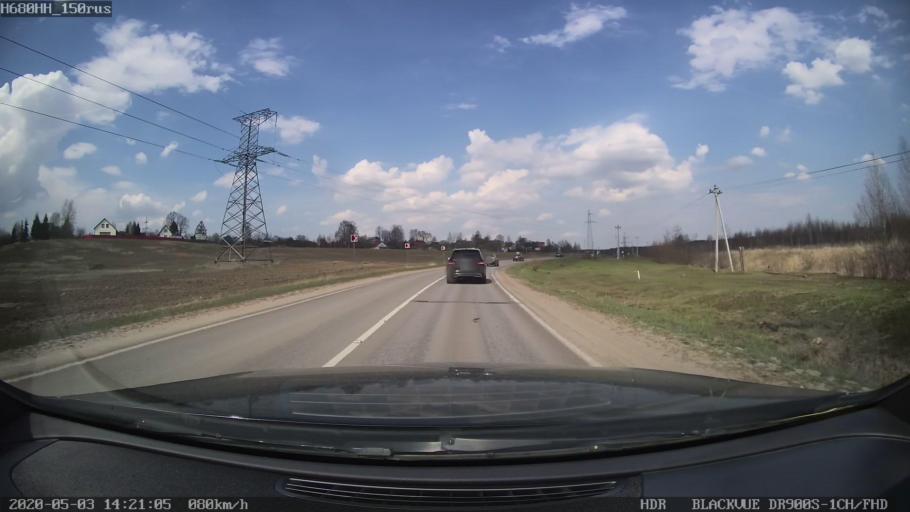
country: RU
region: Moskovskaya
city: Solnechnogorsk
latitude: 56.2524
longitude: 36.9739
